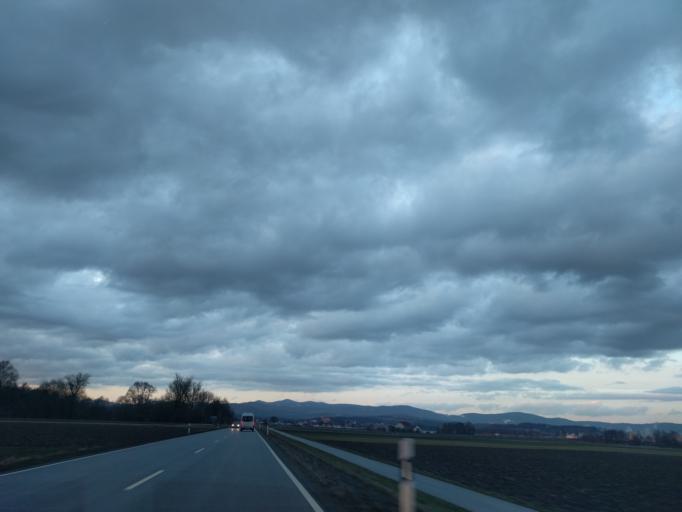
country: DE
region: Bavaria
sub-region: Lower Bavaria
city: Hengersberg
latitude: 48.7470
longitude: 13.0576
